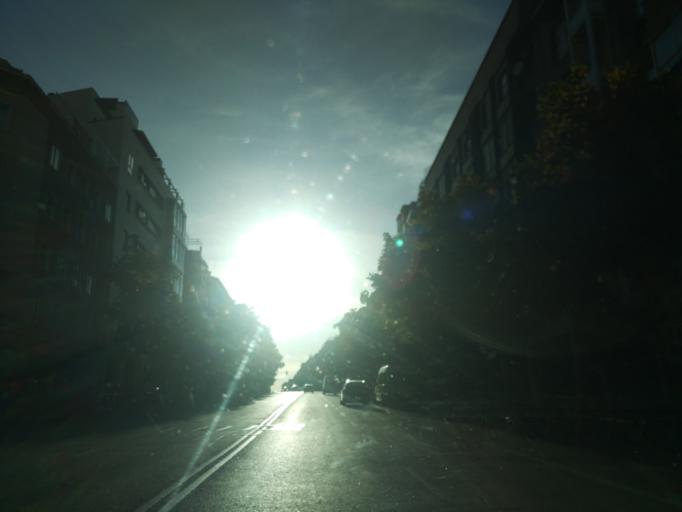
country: ES
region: Madrid
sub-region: Provincia de Madrid
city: Carabanchel
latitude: 40.3924
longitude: -3.7256
